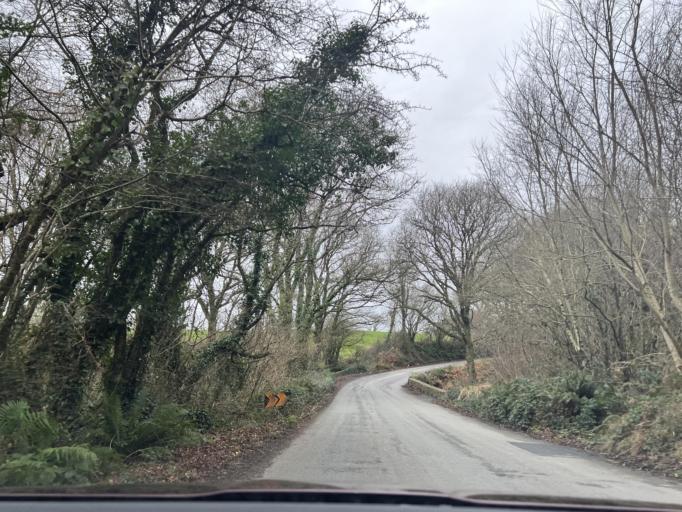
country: IE
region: Leinster
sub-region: Loch Garman
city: Castlebridge
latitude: 52.3799
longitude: -6.5370
